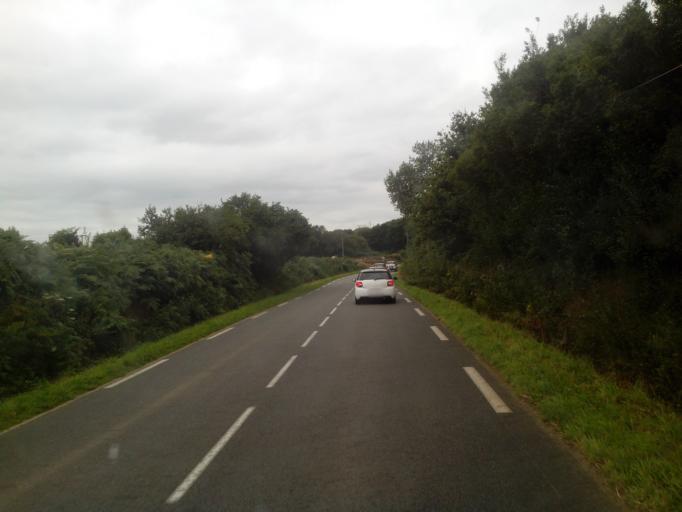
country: FR
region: Brittany
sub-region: Departement des Cotes-d'Armor
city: Plouha
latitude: 48.7006
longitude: -2.9454
